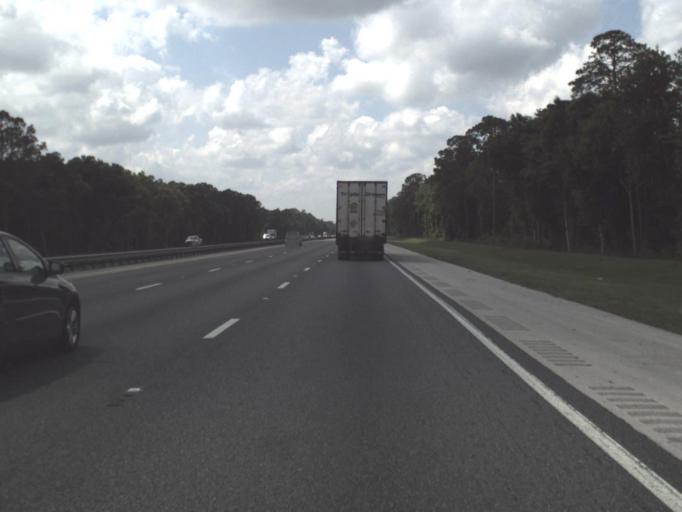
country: US
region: Florida
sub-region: Saint Johns County
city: Saint Augustine
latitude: 29.9407
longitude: -81.4300
